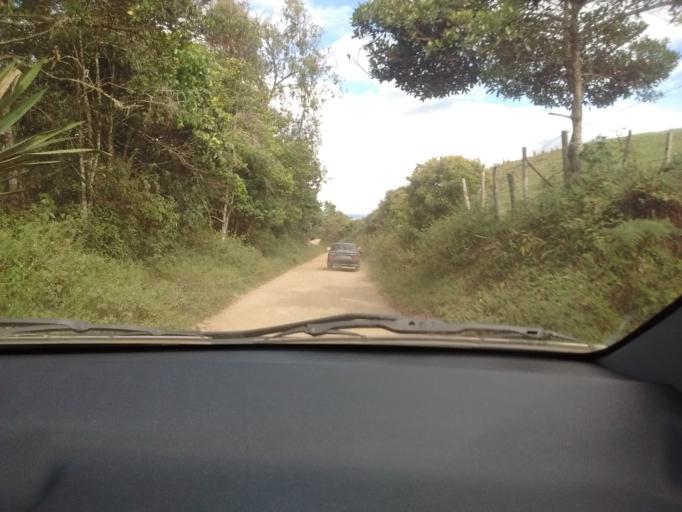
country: CO
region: Cauca
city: El Tambo
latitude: 2.4616
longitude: -76.8228
